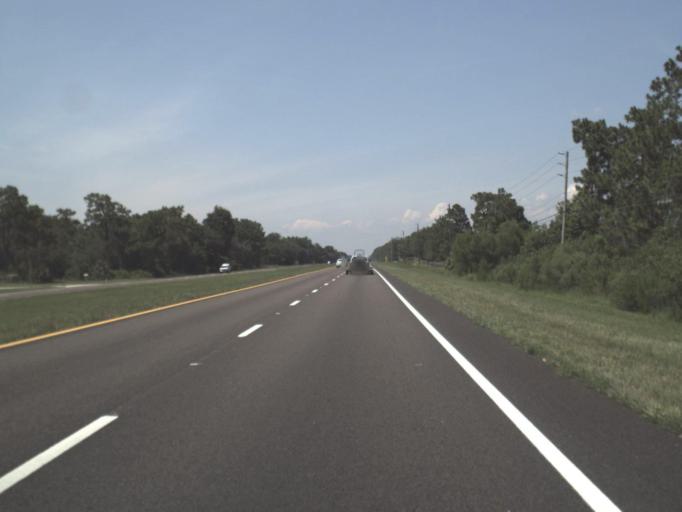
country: US
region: Florida
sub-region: Citrus County
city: Sugarmill Woods
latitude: 28.7042
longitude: -82.5524
